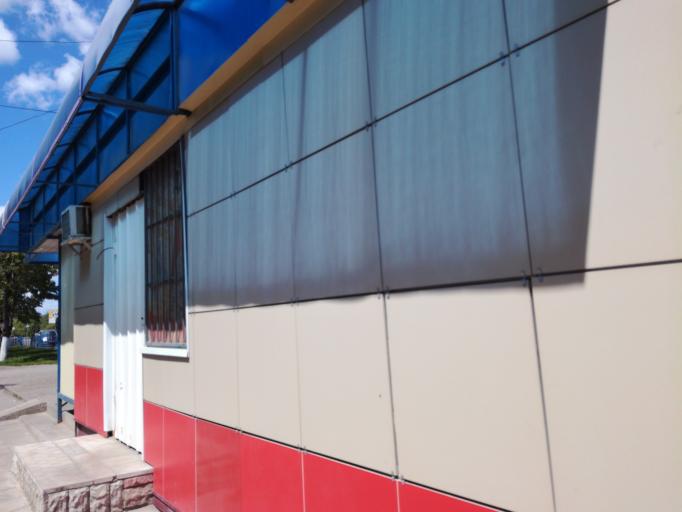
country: RU
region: Kursk
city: Kursk
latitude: 51.7455
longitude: 36.2581
